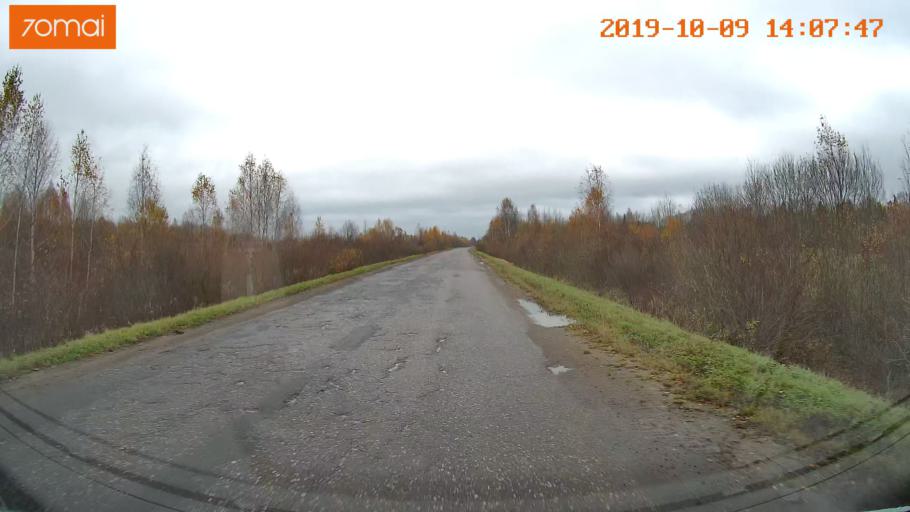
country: RU
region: Kostroma
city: Buy
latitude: 58.4728
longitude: 41.4273
